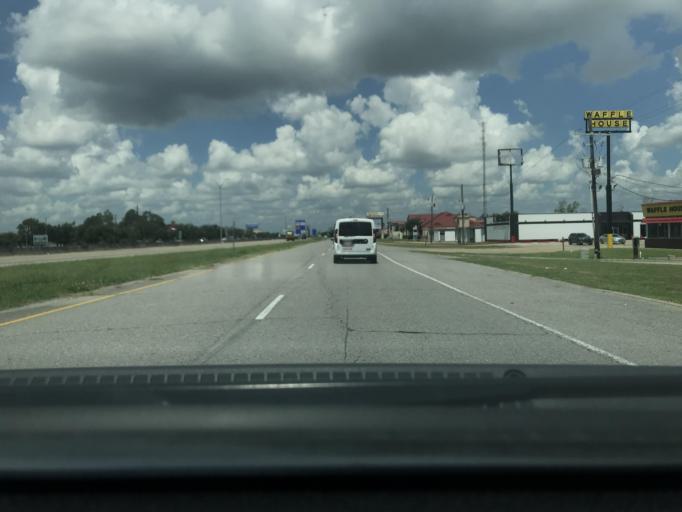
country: US
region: Louisiana
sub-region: Calcasieu Parish
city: Westlake
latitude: 30.2374
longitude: -93.2249
